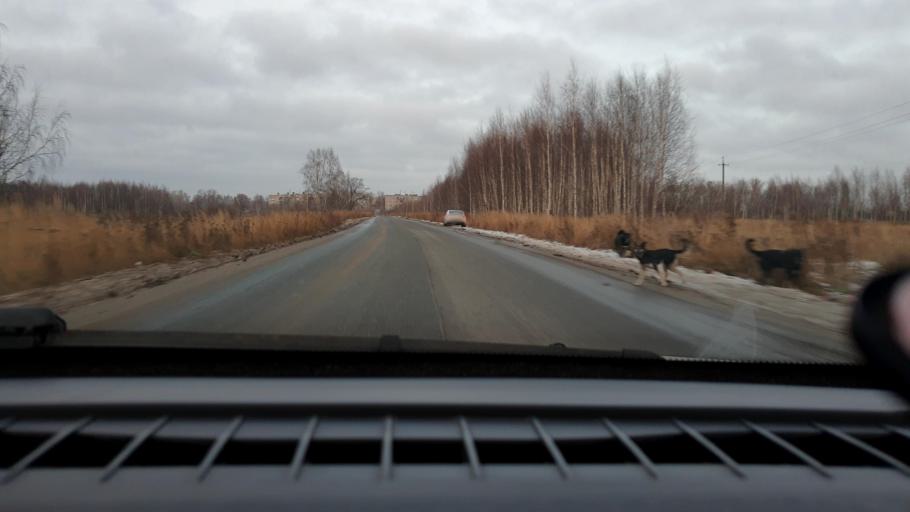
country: RU
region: Nizjnij Novgorod
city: Gorbatovka
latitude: 56.2394
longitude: 43.7426
